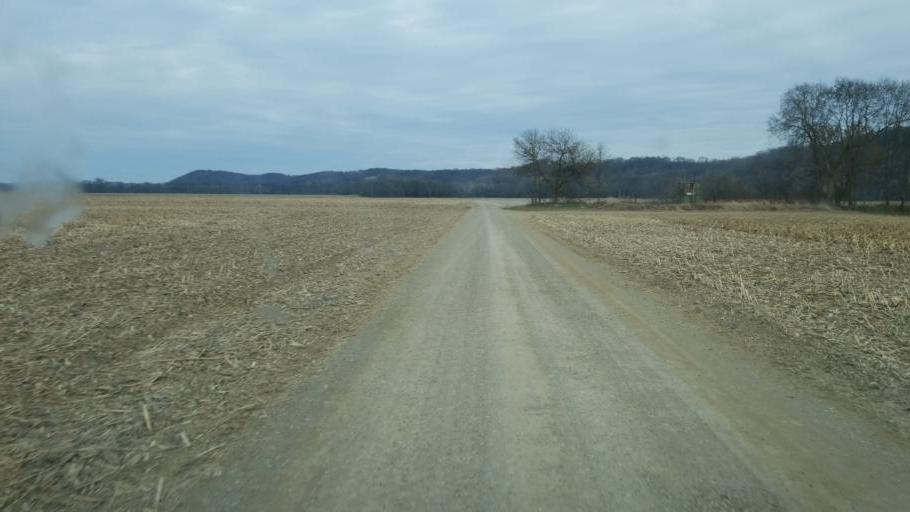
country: US
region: Ohio
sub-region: Muskingum County
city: Dresden
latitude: 40.1383
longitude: -81.9594
